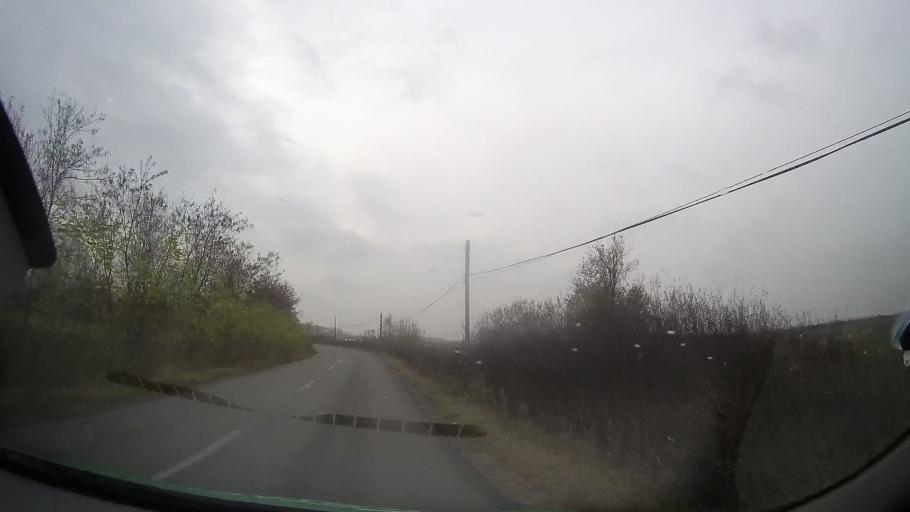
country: RO
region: Prahova
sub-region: Comuna Gherghita
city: Gherghita
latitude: 44.8190
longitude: 26.2710
